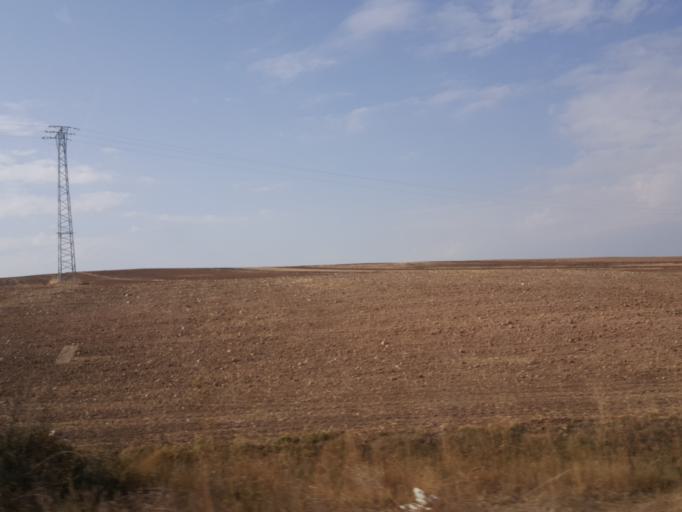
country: TR
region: Corum
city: Cemilbey
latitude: 40.1740
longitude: 35.0442
